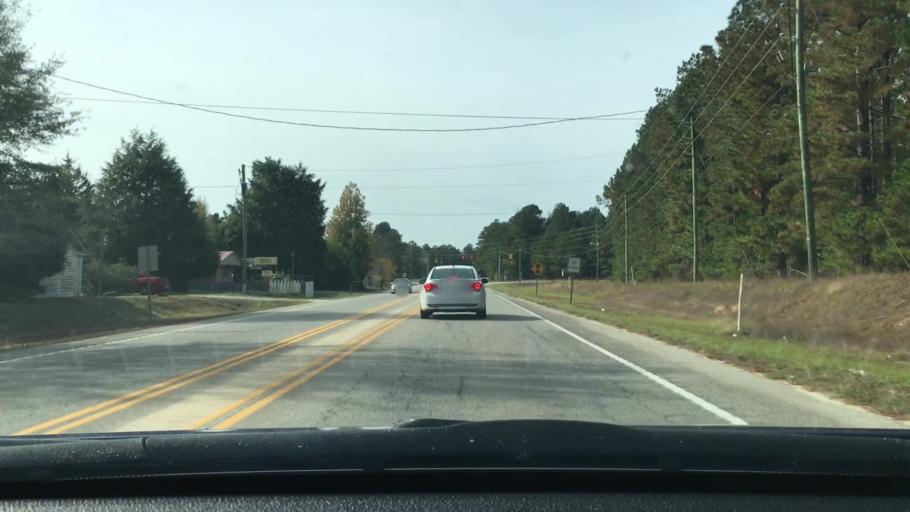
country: US
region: South Carolina
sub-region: Sumter County
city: Cherryvale
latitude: 33.9367
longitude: -80.4509
